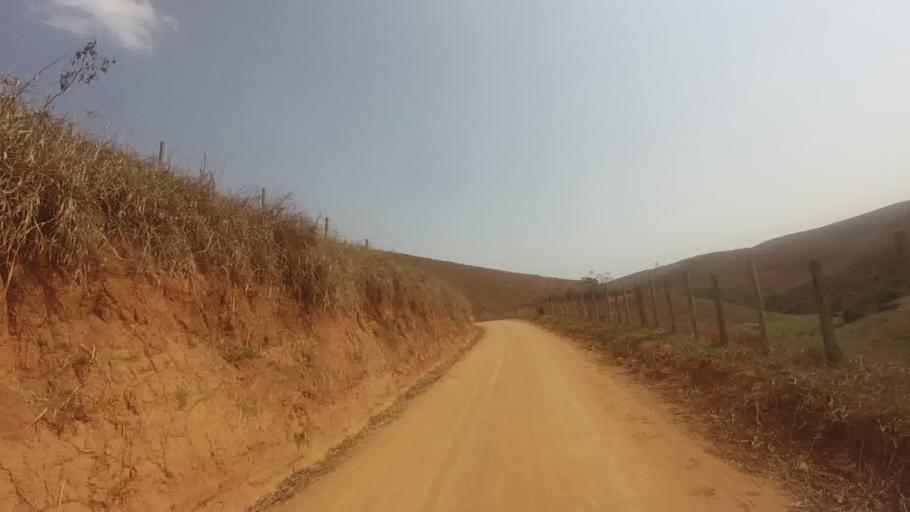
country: BR
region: Espirito Santo
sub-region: Sao Jose Do Calcado
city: Sao Jose do Calcado
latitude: -21.0629
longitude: -41.5419
